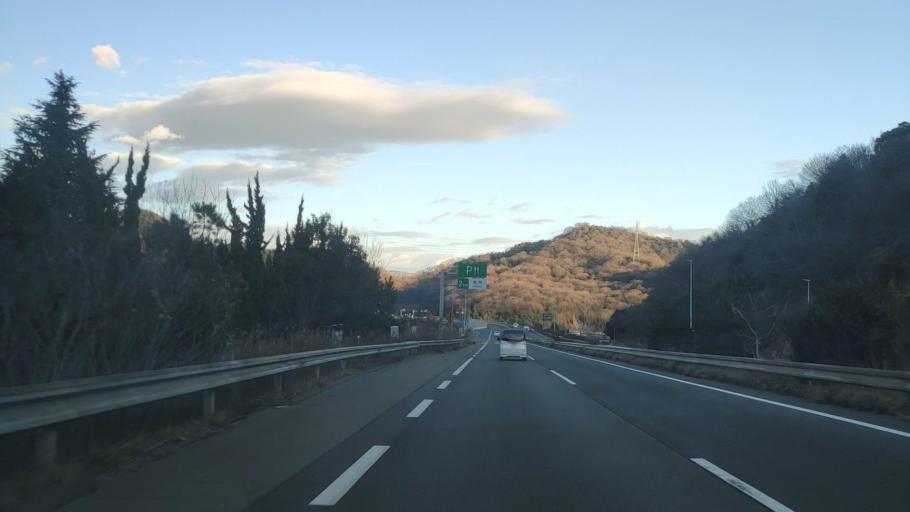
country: JP
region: Hyogo
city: Tatsunocho-tominaga
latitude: 34.8354
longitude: 134.6180
